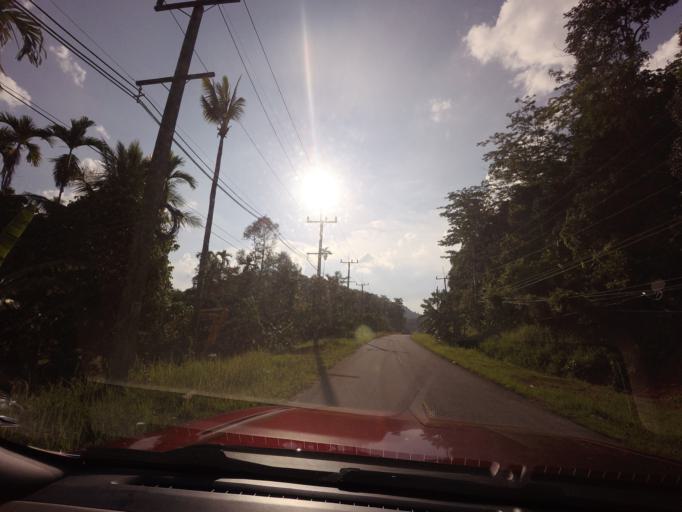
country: TH
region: Yala
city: Than To
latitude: 6.1931
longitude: 101.2459
